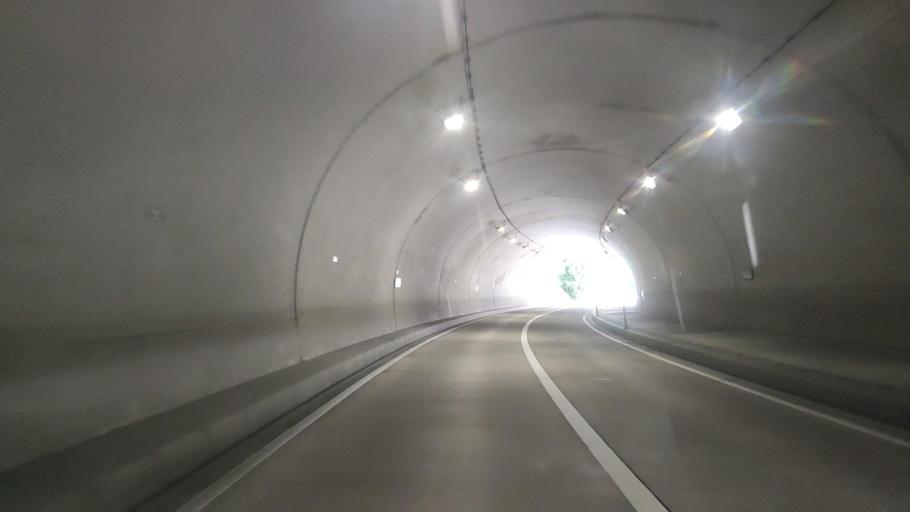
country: JP
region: Shiga Prefecture
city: Nagahama
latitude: 35.3836
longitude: 136.3338
